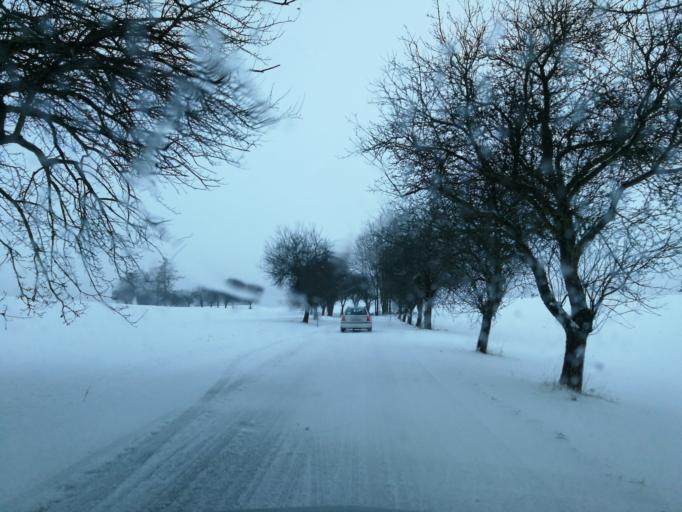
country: CZ
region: Vysocina
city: Heralec
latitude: 49.5331
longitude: 15.4311
